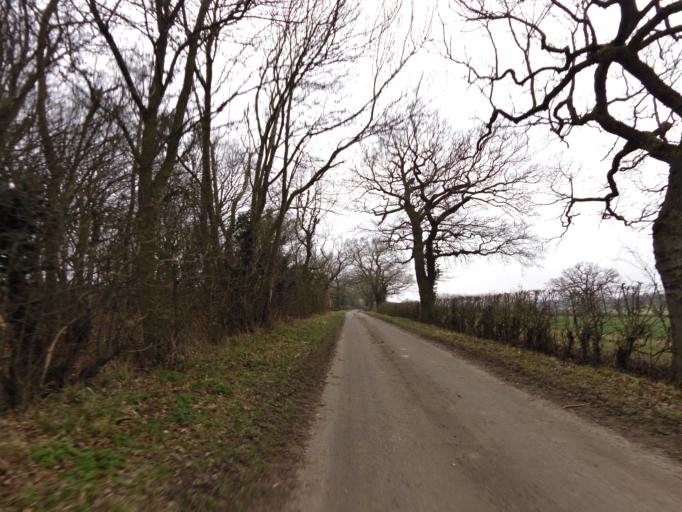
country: GB
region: England
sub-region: Suffolk
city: Cookley
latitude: 52.2543
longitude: 1.4144
